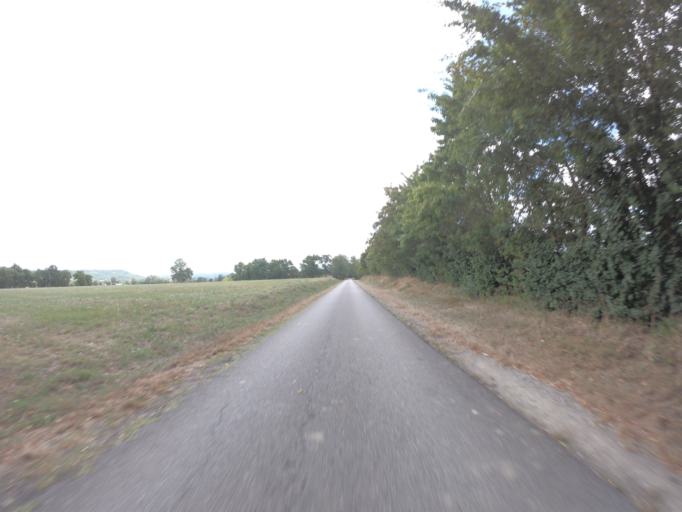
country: FR
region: Midi-Pyrenees
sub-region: Departement de l'Ariege
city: La Tour-du-Crieu
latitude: 43.1043
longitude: 1.7262
